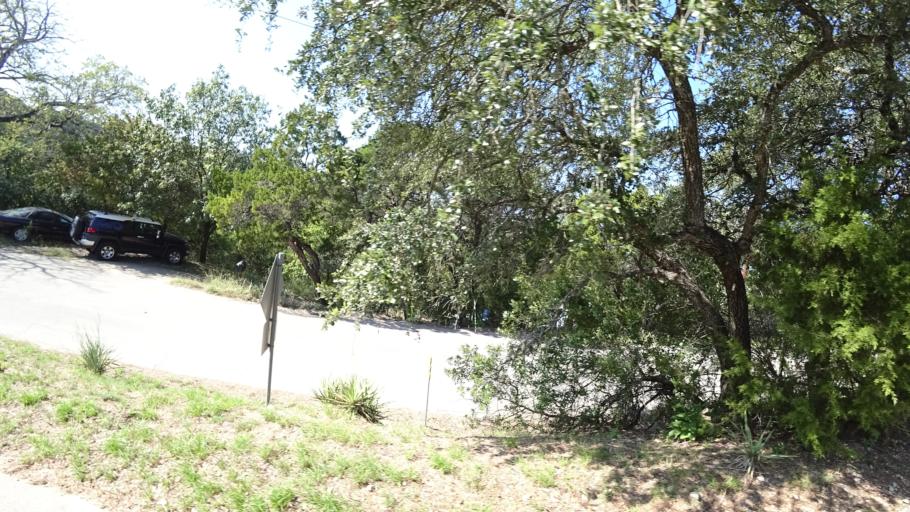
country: US
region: Texas
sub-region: Travis County
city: West Lake Hills
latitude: 30.3031
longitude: -97.8067
